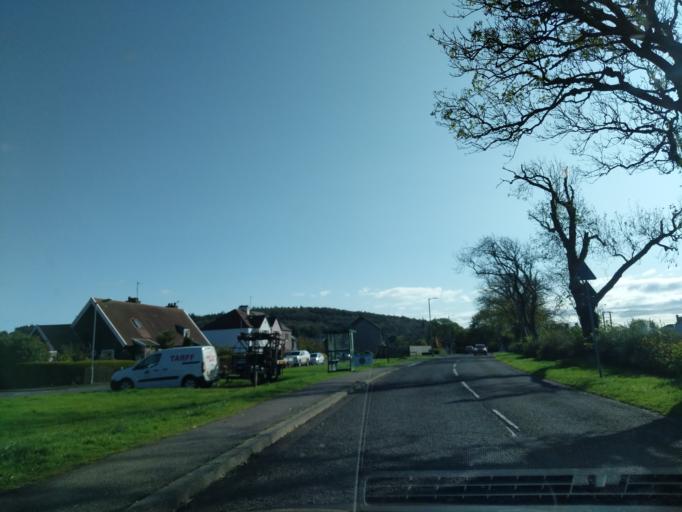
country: GB
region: Scotland
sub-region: Dumfries and Galloway
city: Kirkcudbright
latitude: 54.8417
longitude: -4.0540
